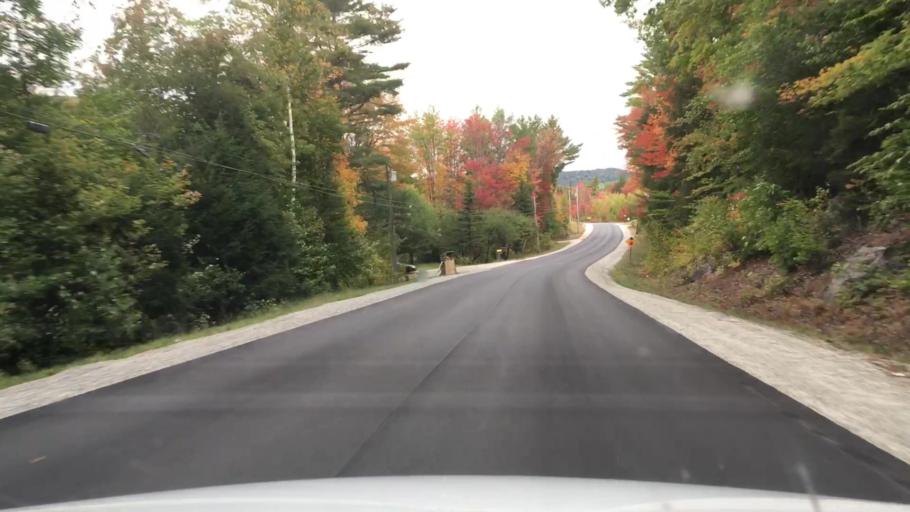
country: US
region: Maine
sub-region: Oxford County
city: Bethel
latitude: 44.3221
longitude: -70.7673
